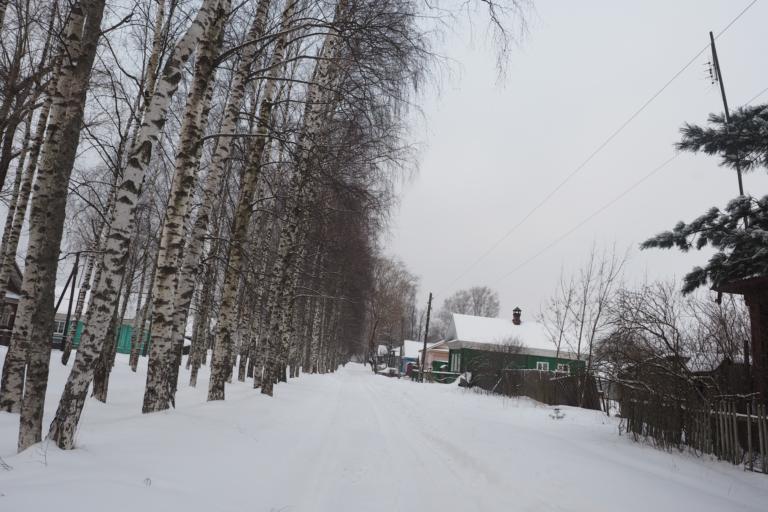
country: RU
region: Tverskaya
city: Ves'yegonsk
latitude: 58.6632
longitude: 37.2681
